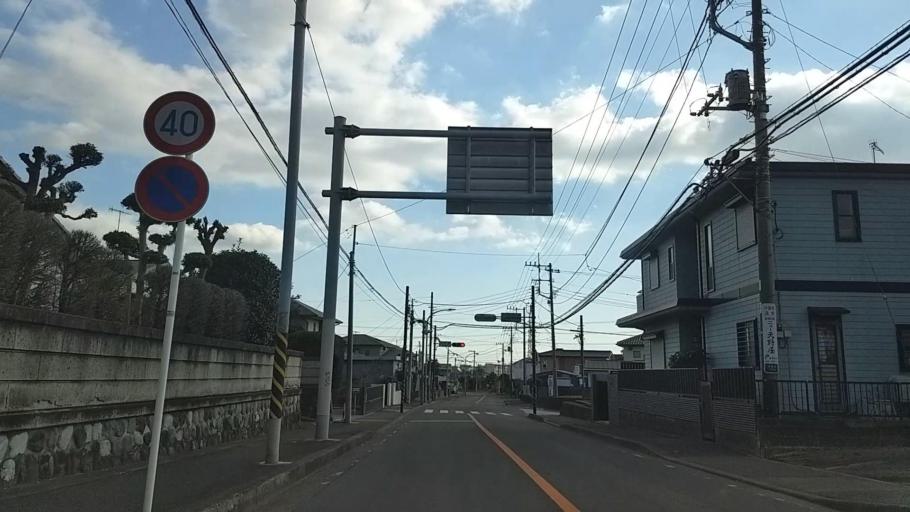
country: JP
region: Kanagawa
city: Isehara
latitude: 35.4207
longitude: 139.2959
